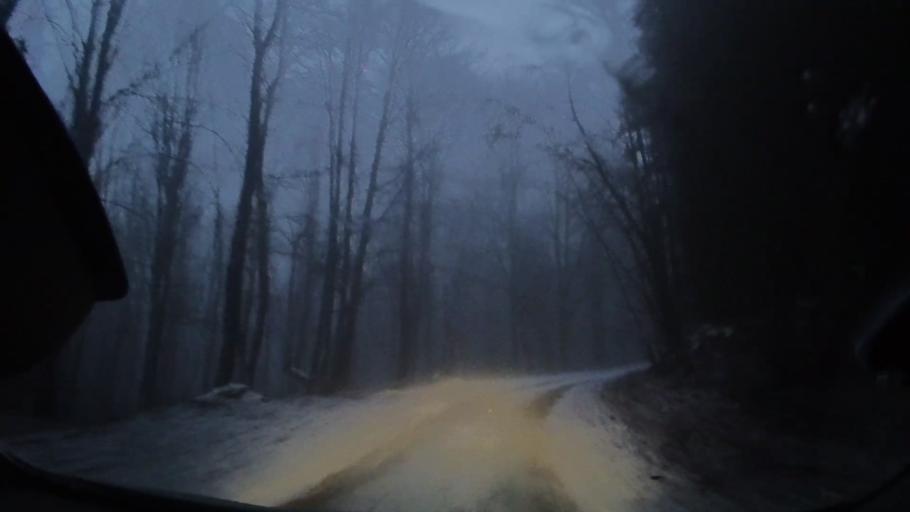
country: RO
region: Alba
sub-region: Comuna Avram Iancu
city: Avram Iancu
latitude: 46.3149
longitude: 22.7992
